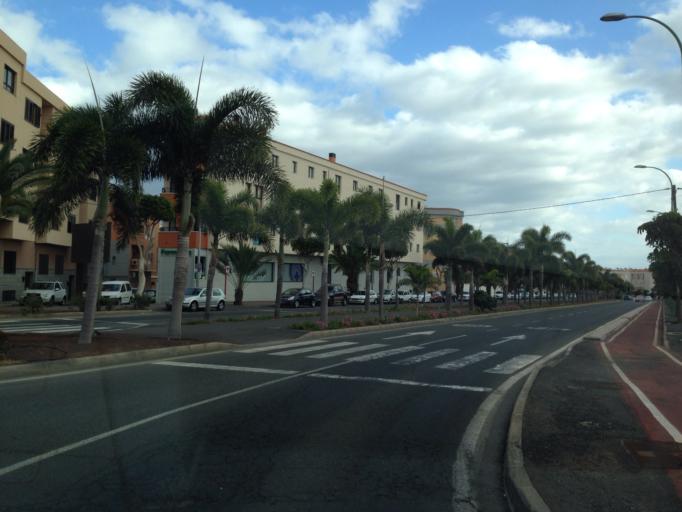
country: ES
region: Canary Islands
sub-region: Provincia de Las Palmas
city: Cruce de Arinaga
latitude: 27.8394
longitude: -15.4533
